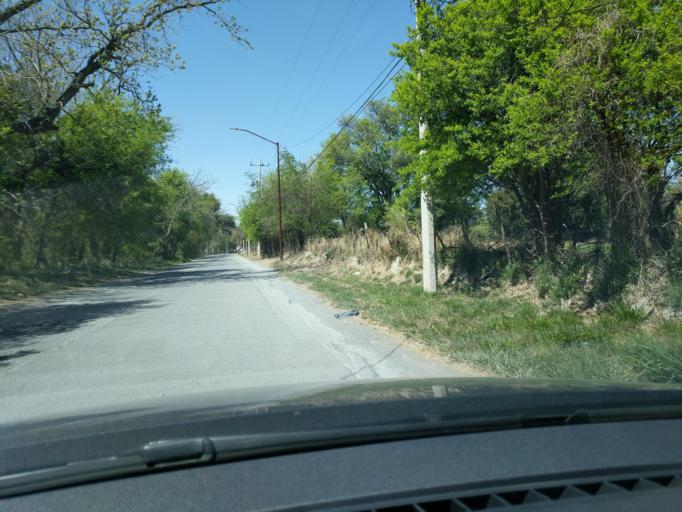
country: MX
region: Nuevo Leon
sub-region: Apodaca
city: Artemio Trevino
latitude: 25.8119
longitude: -100.1298
